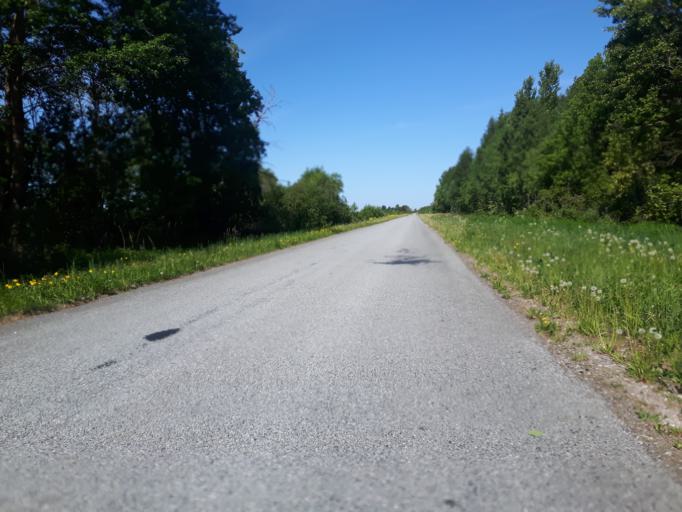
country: EE
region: Ida-Virumaa
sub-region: Aseri vald
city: Aseri
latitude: 59.4583
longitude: 26.8389
